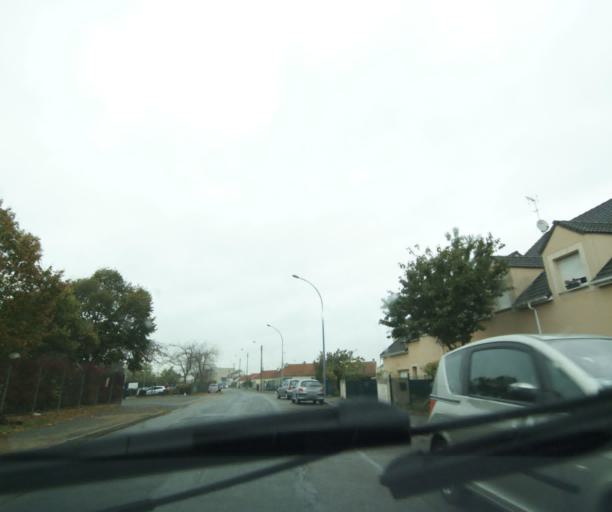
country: FR
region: Centre
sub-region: Departement d'Eure-et-Loir
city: Vernouillet
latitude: 48.7219
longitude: 1.3730
